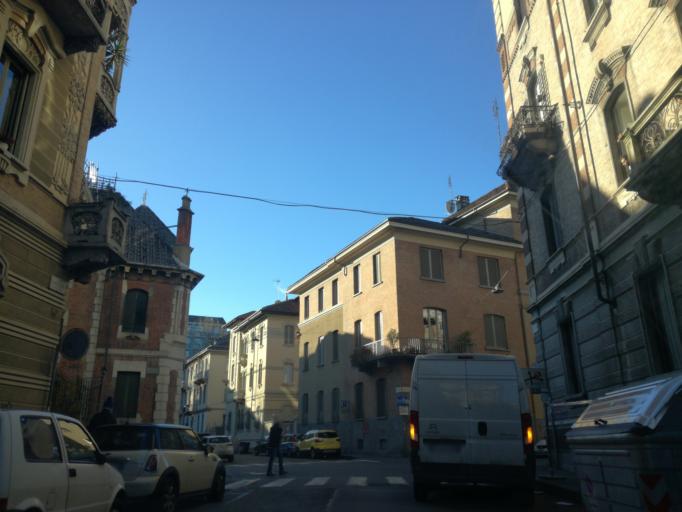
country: IT
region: Piedmont
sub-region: Provincia di Torino
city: Turin
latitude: 45.0777
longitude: 7.6657
